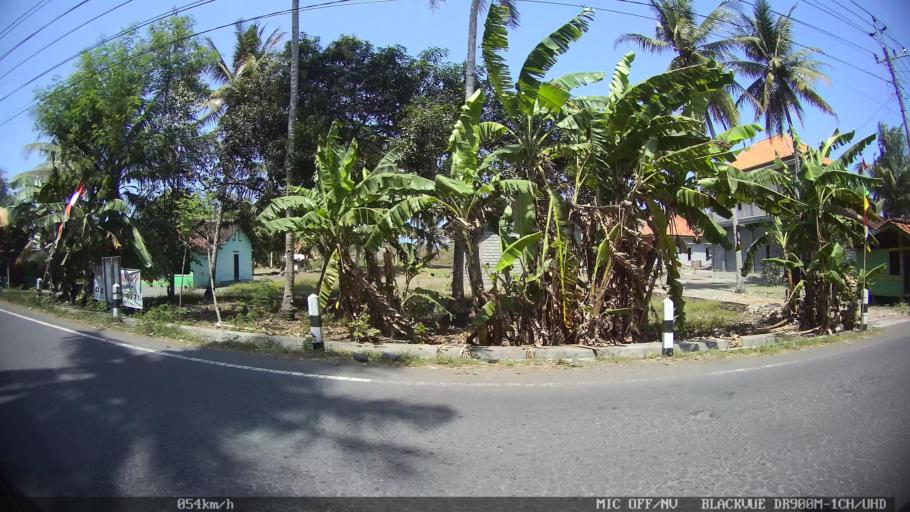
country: ID
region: Daerah Istimewa Yogyakarta
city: Srandakan
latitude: -7.9287
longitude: 110.1322
